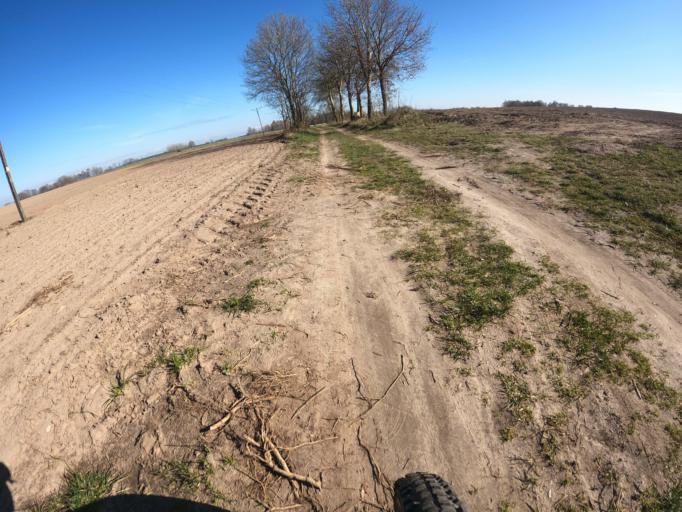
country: PL
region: West Pomeranian Voivodeship
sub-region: Powiat kolobrzeski
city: Ryman
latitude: 54.0198
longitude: 15.4742
